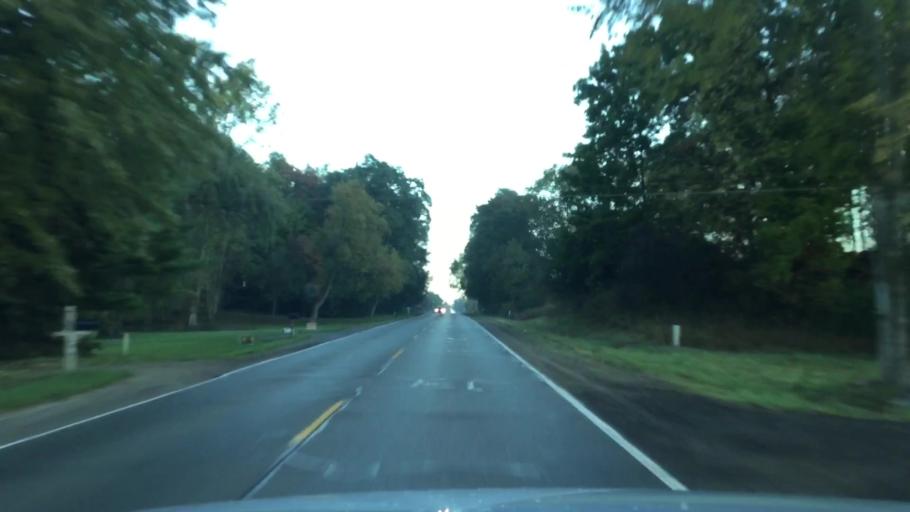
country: US
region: Michigan
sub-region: Livingston County
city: Howell
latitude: 42.6573
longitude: -83.9355
